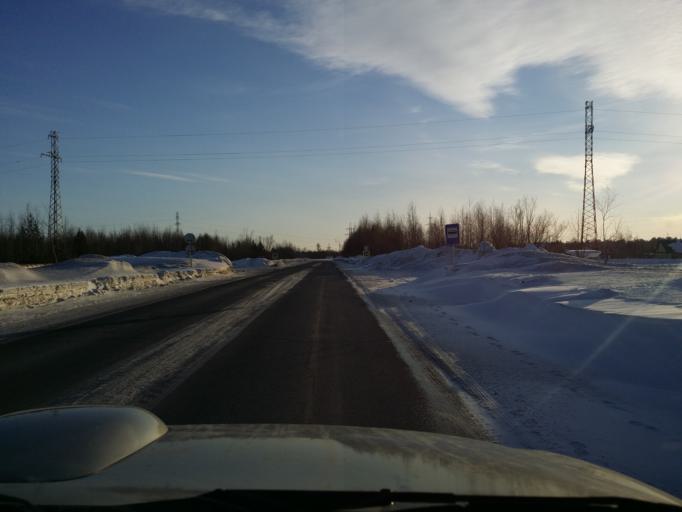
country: RU
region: Khanty-Mansiyskiy Avtonomnyy Okrug
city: Izluchinsk
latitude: 60.9673
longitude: 76.8860
